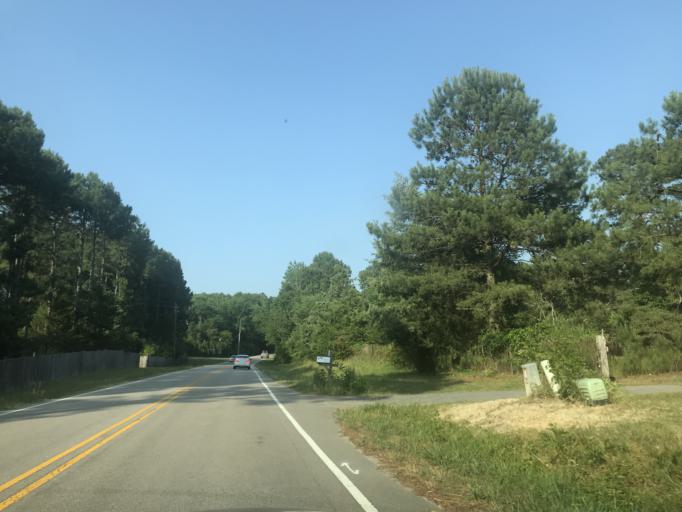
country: US
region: North Carolina
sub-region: Wake County
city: Rolesville
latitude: 35.8606
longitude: -78.4930
